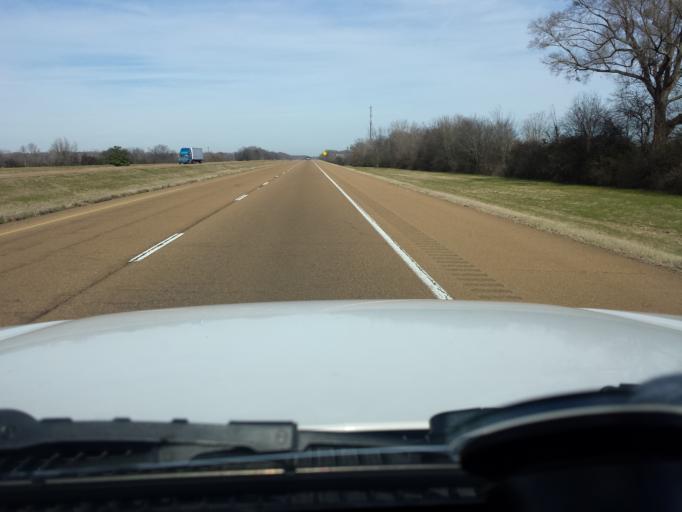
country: US
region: Mississippi
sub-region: Madison County
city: Canton
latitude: 32.6276
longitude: -90.0624
